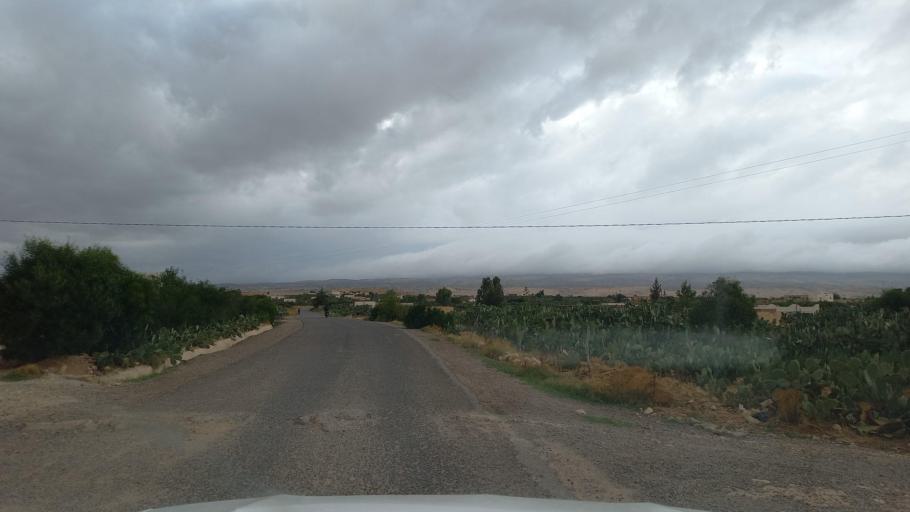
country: TN
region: Al Qasrayn
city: Kasserine
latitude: 35.2771
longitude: 8.9510
